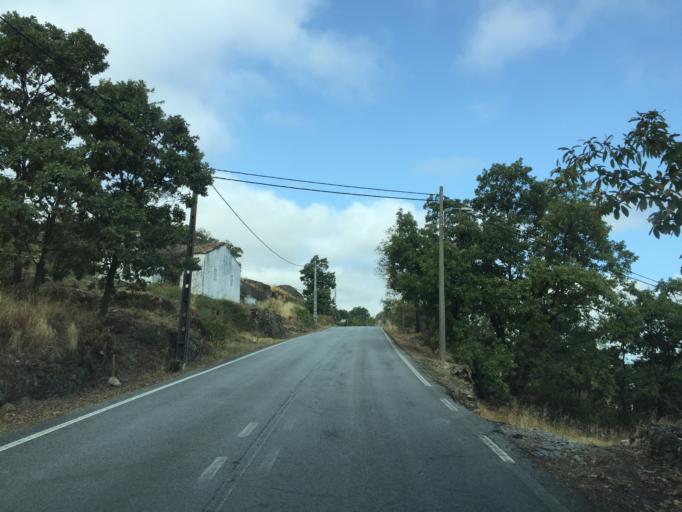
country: PT
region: Portalegre
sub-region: Marvao
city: Marvao
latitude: 39.4011
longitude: -7.3752
